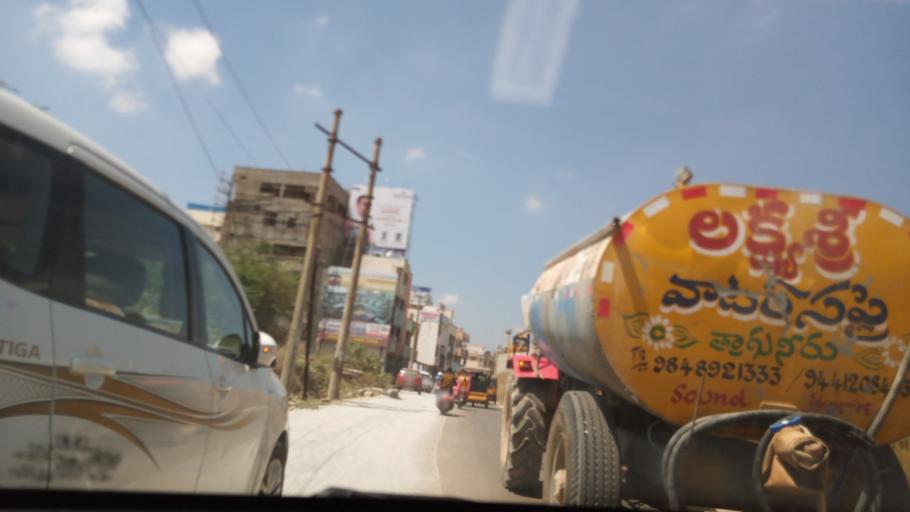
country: IN
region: Andhra Pradesh
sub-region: Chittoor
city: Akkarampalle
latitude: 13.6431
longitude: 79.4334
